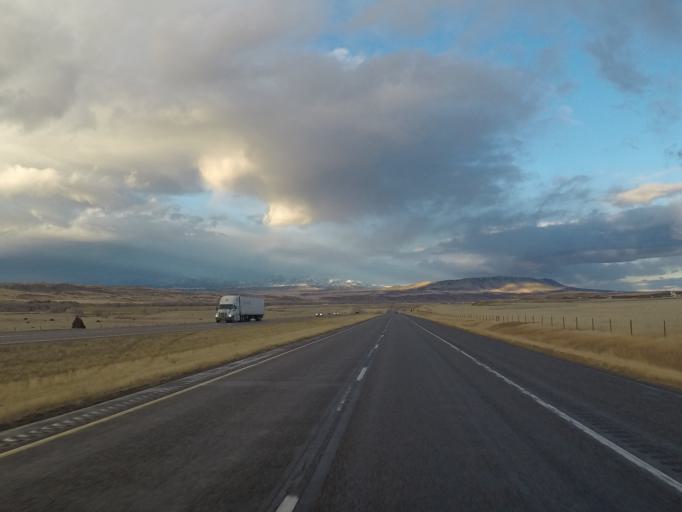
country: US
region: Montana
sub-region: Park County
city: Livingston
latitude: 45.6672
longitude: -110.5242
